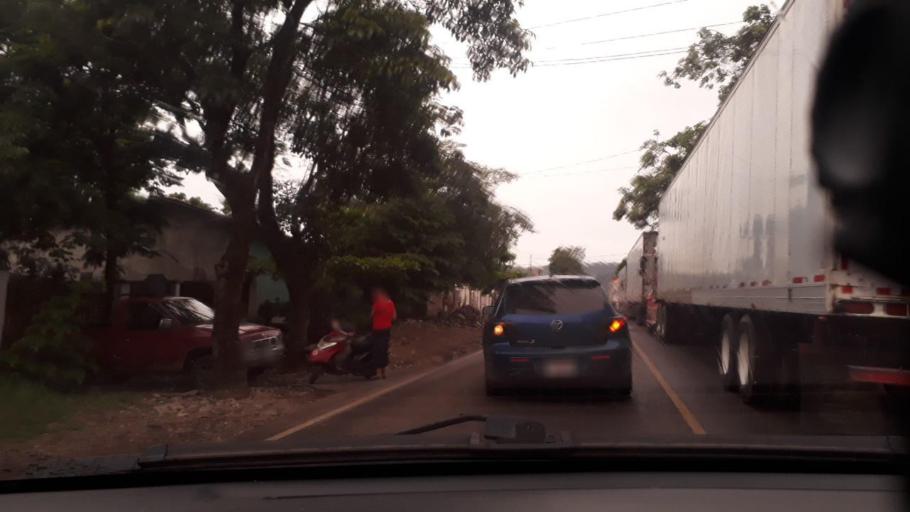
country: GT
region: Jutiapa
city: Atescatempa
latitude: 14.1930
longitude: -89.6725
